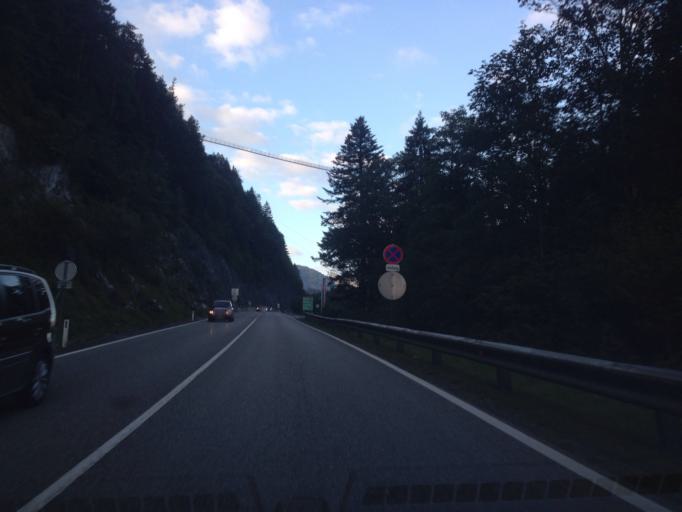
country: AT
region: Tyrol
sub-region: Politischer Bezirk Reutte
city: Reutte
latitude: 47.4669
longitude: 10.7238
